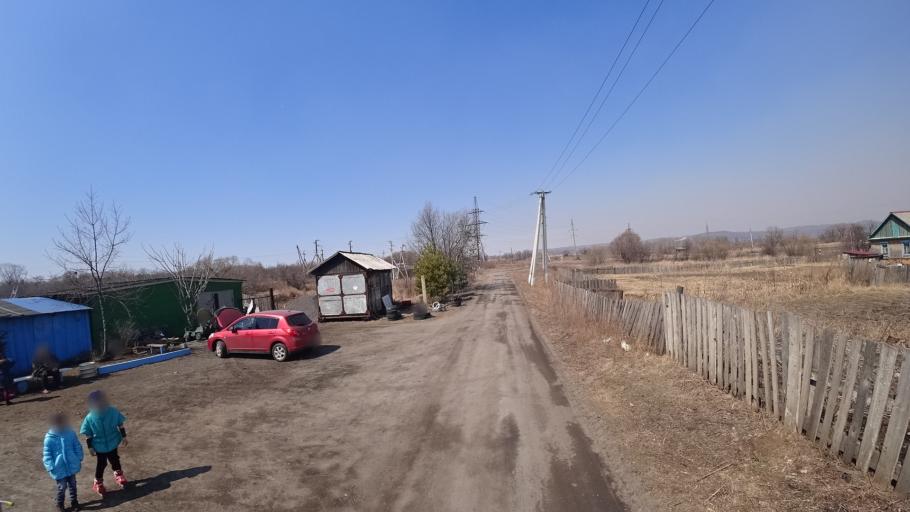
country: RU
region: Amur
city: Novobureyskiy
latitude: 49.7889
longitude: 129.8403
